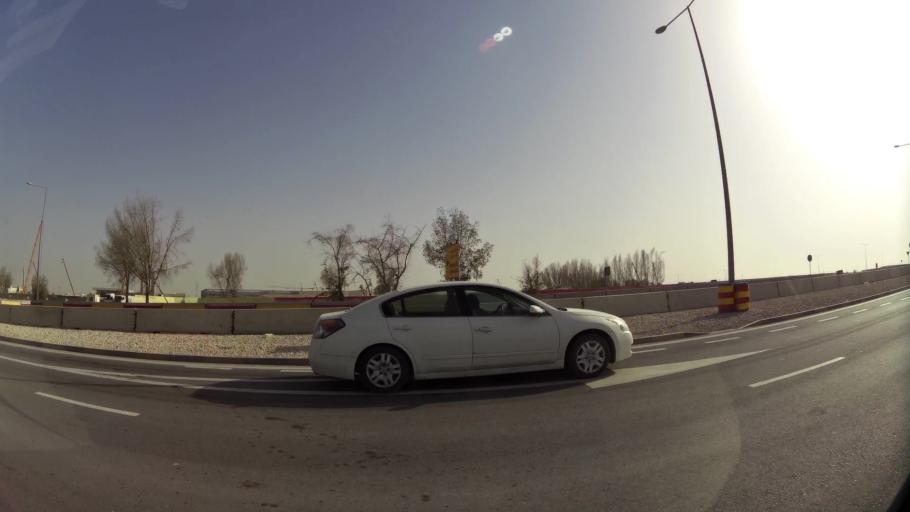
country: QA
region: Baladiyat ar Rayyan
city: Ar Rayyan
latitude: 25.3193
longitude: 51.4233
